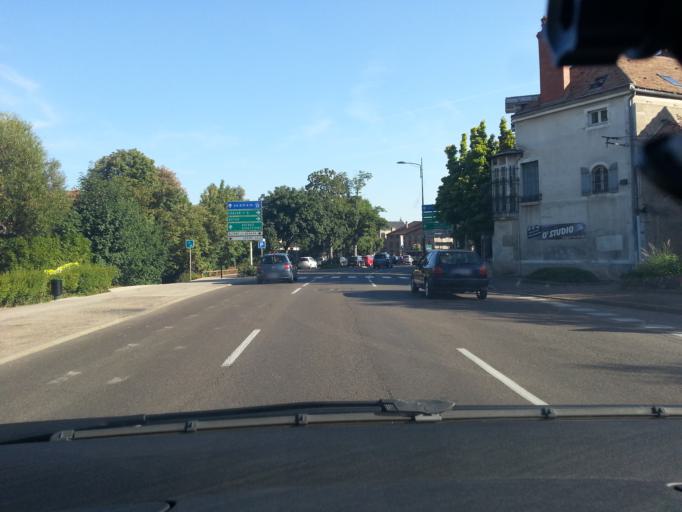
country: FR
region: Bourgogne
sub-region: Departement de la Cote-d'Or
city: Beaune
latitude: 47.0235
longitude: 4.8329
